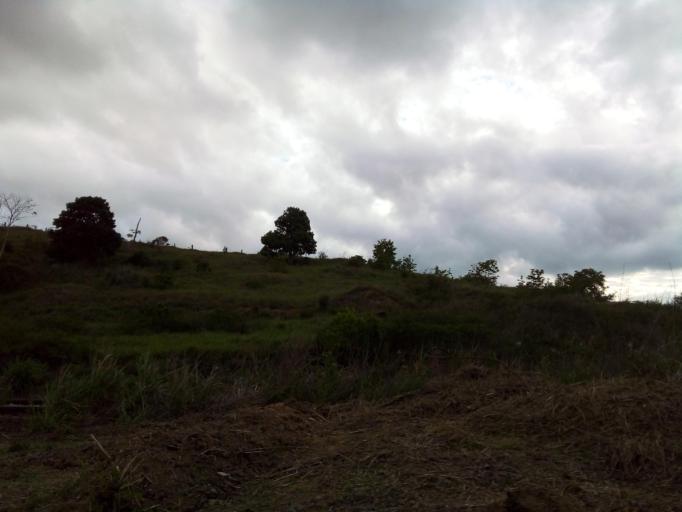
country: BR
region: Espirito Santo
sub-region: Marilandia
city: Marilandia
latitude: -19.5459
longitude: -40.4561
